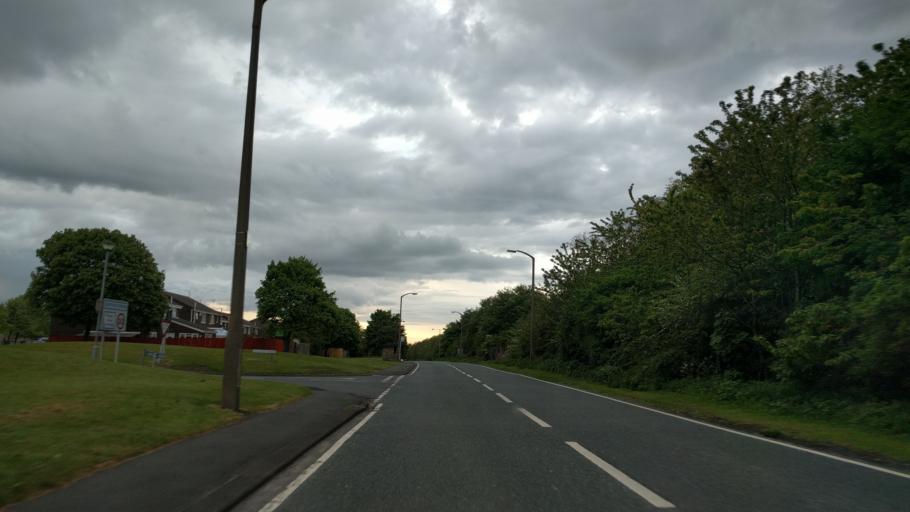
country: GB
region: England
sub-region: Northumberland
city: Cramlington
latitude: 55.0890
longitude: -1.5680
